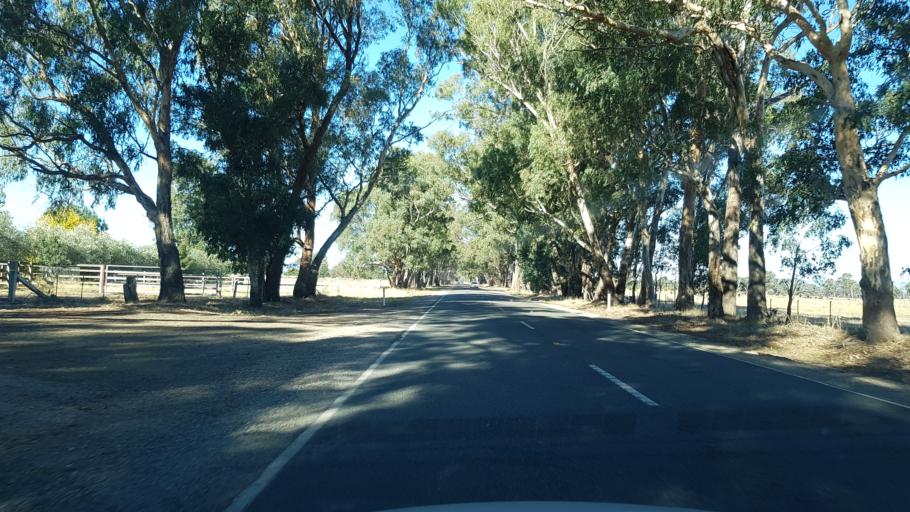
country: AU
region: Victoria
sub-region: Wangaratta
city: Wangaratta
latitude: -36.4347
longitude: 146.3146
